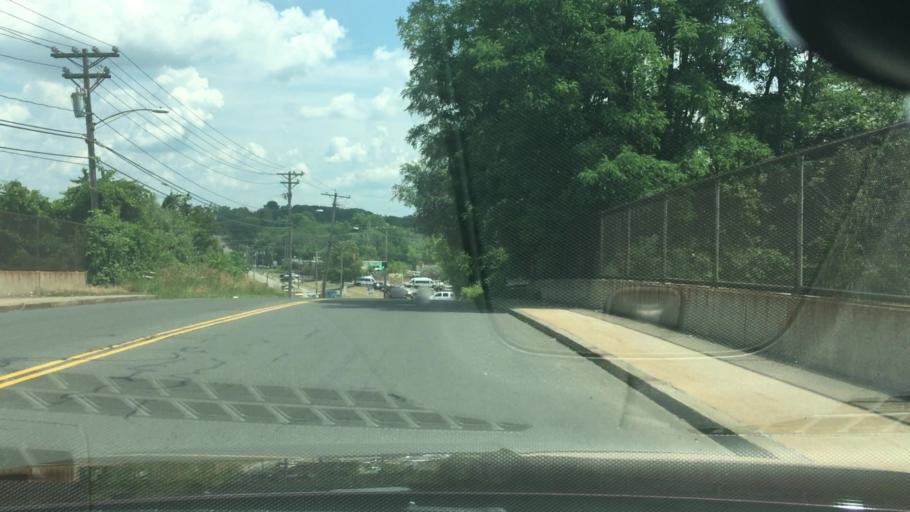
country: US
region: Connecticut
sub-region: Hartford County
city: Kensington
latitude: 41.6541
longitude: -72.7519
